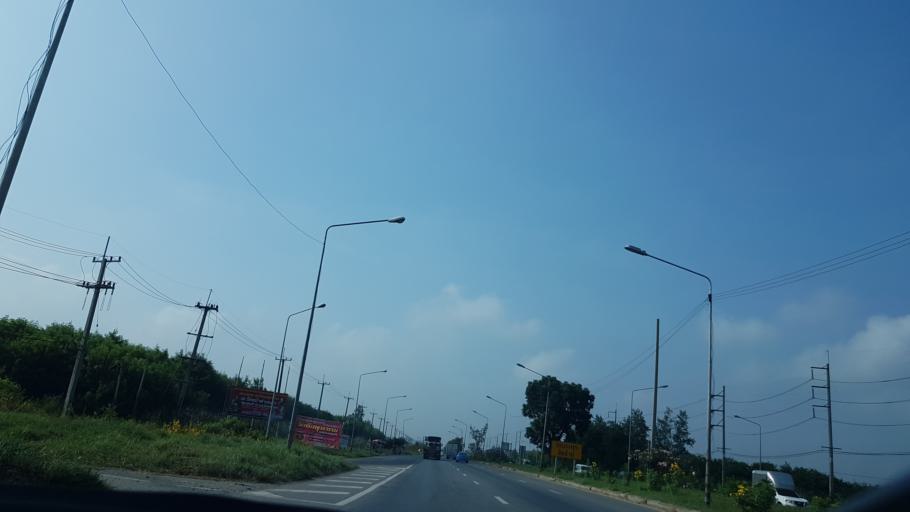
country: TH
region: Pathum Thani
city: Sam Khok
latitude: 14.1297
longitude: 100.5386
